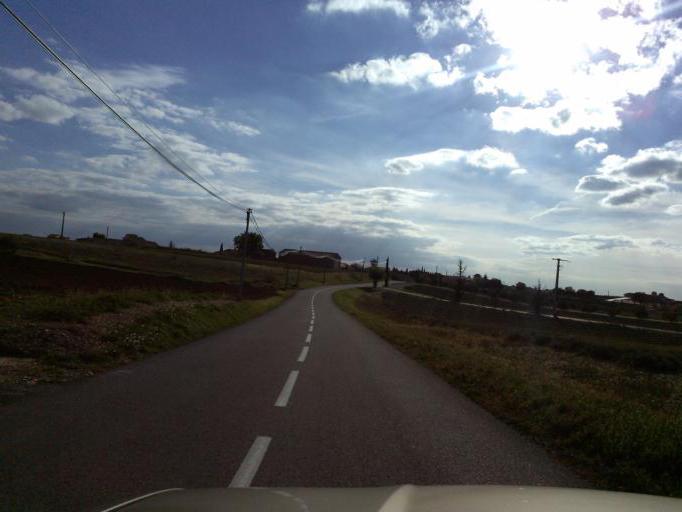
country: FR
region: Provence-Alpes-Cote d'Azur
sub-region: Departement des Alpes-de-Haute-Provence
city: Valensole
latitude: 43.8445
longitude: 5.9872
